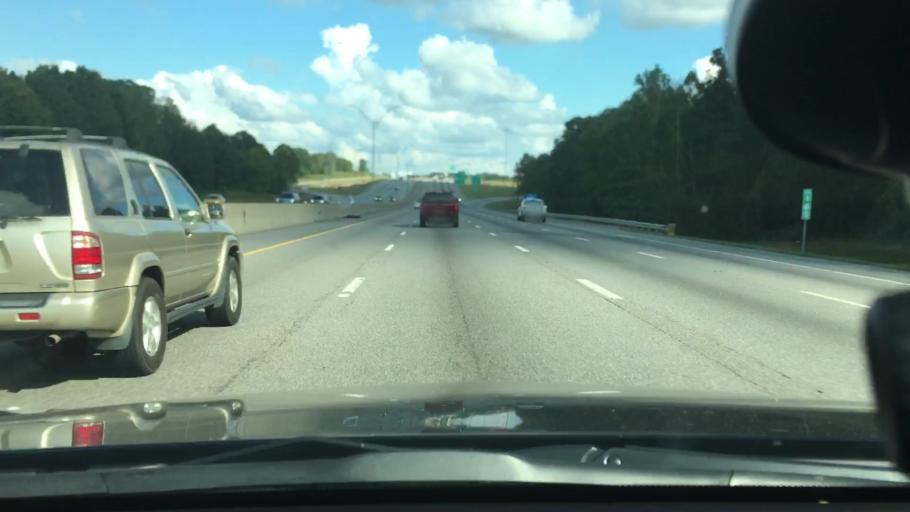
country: US
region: North Carolina
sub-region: Orange County
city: Hillsborough
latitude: 36.0738
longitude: -79.1762
